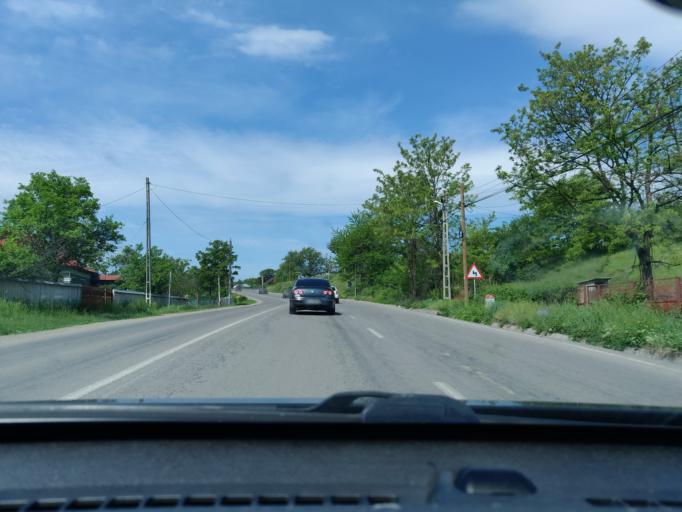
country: RO
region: Vrancea
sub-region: Comuna Vidra
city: Vidra
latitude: 45.9096
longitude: 26.9150
